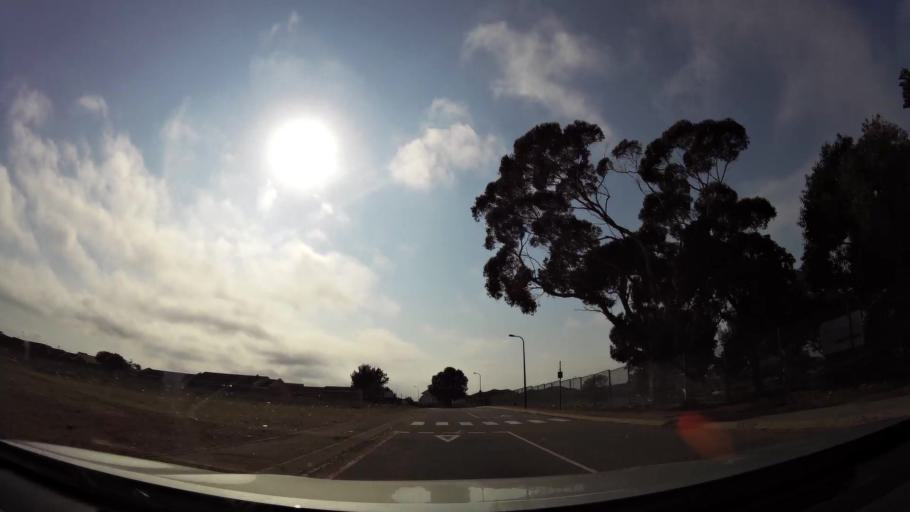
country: ZA
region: Eastern Cape
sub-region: Nelson Mandela Bay Metropolitan Municipality
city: Port Elizabeth
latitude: -33.9207
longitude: 25.5344
